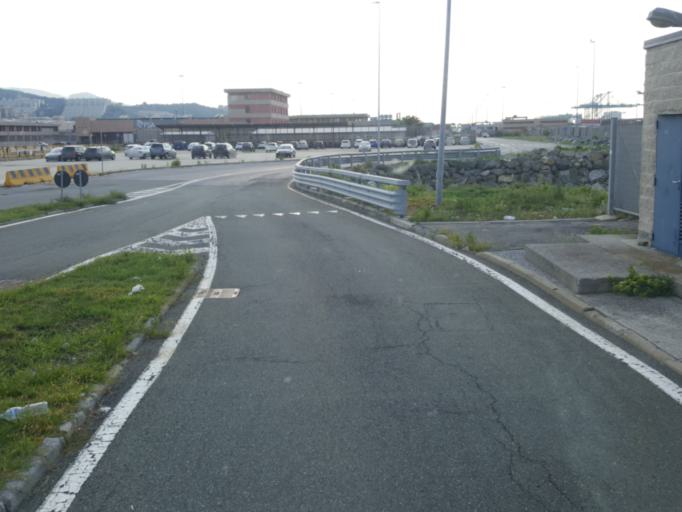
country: IT
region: Liguria
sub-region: Provincia di Genova
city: Mele
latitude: 44.4244
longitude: 8.7686
